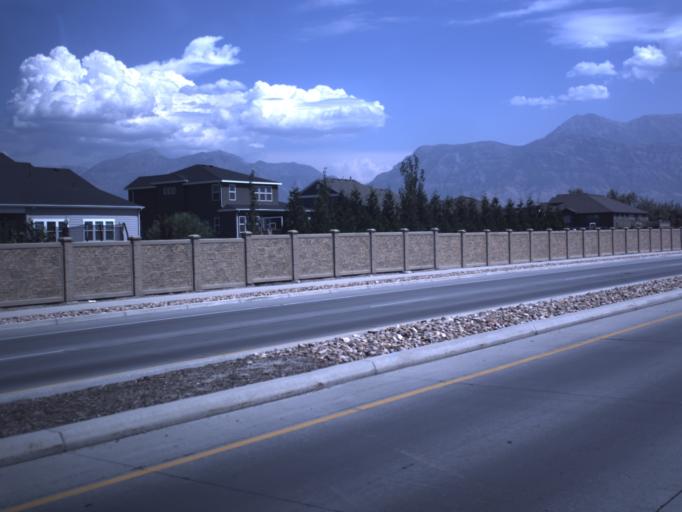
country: US
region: Utah
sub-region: Utah County
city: Lehi
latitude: 40.3736
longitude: -111.8546
